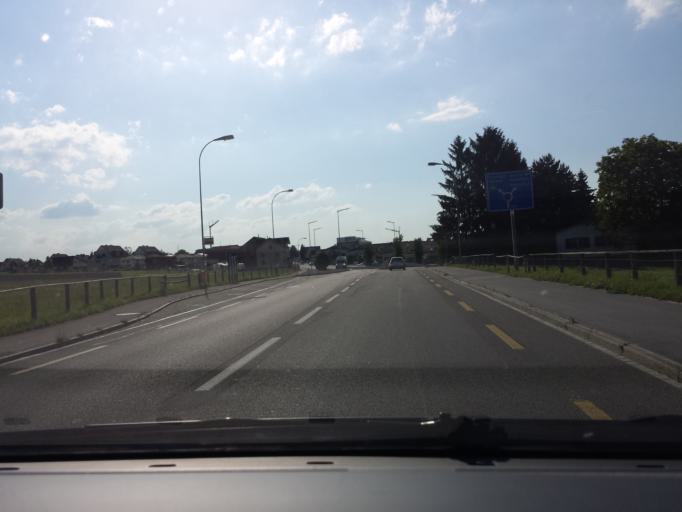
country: CH
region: Thurgau
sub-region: Arbon District
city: Arbon
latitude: 47.5208
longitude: 9.4151
